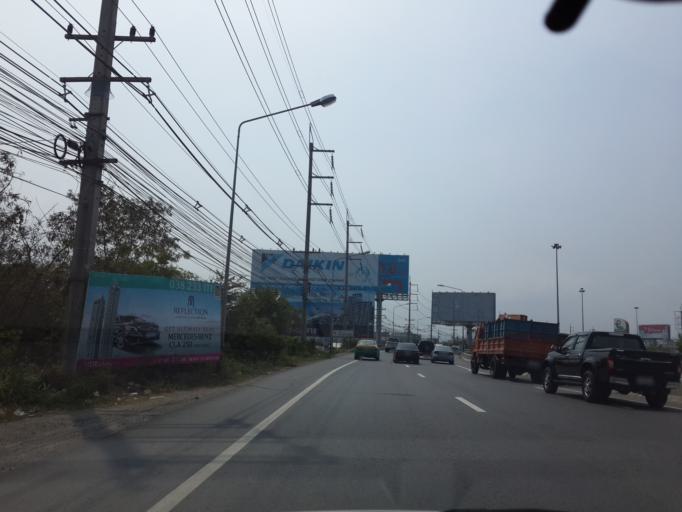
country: TH
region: Chon Buri
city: Chon Buri
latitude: 13.4305
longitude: 101.0031
